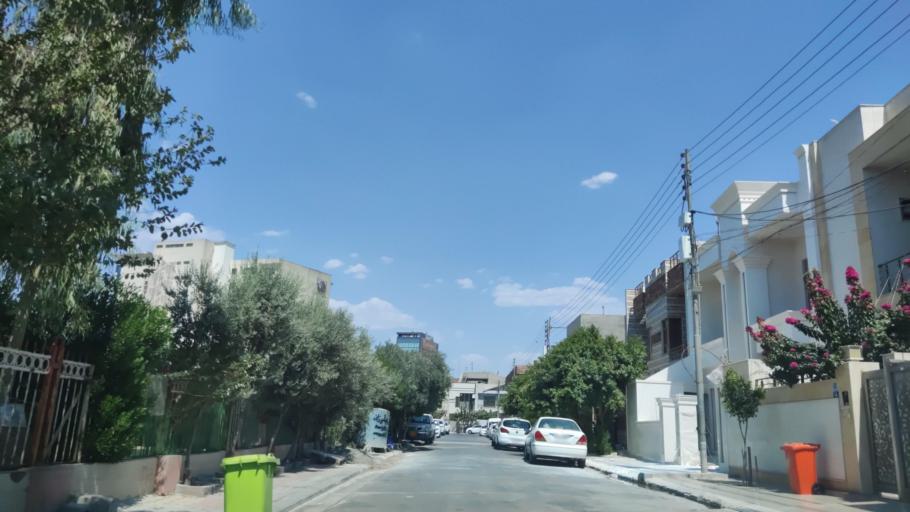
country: IQ
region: Arbil
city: Erbil
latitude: 36.1971
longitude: 44.0216
